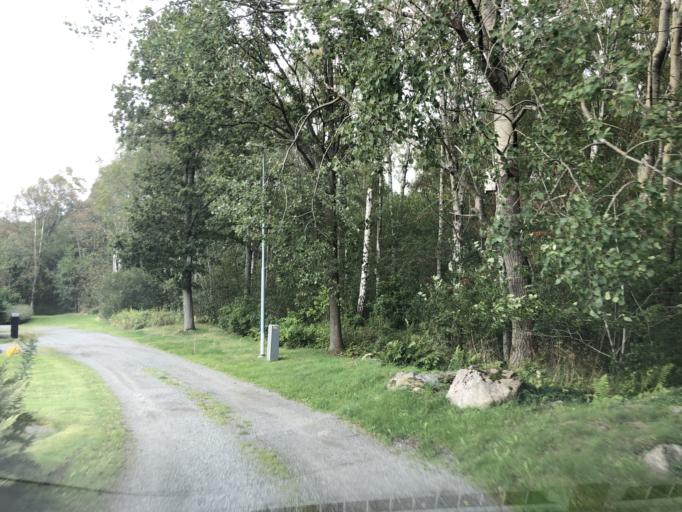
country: SE
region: Vaestra Goetaland
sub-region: Goteborg
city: Majorna
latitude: 57.7497
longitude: 11.8866
